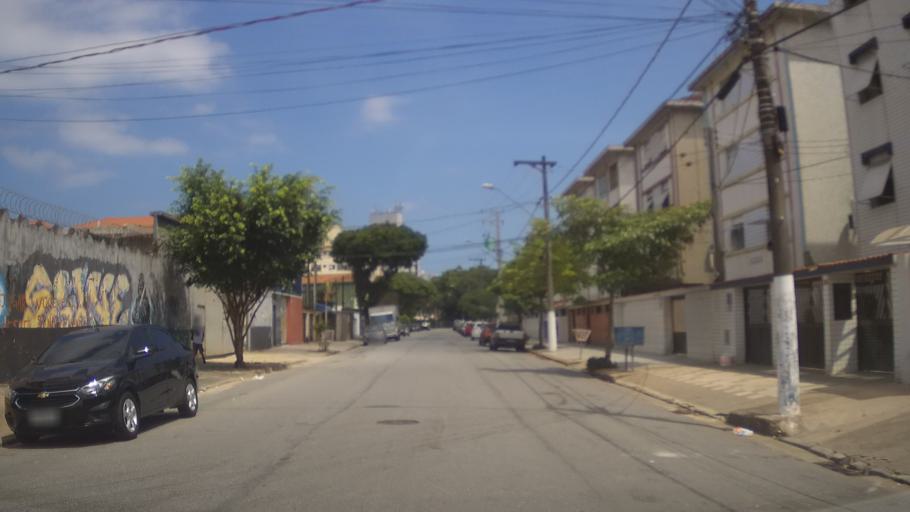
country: BR
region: Sao Paulo
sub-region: Santos
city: Santos
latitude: -23.9633
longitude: -46.3106
